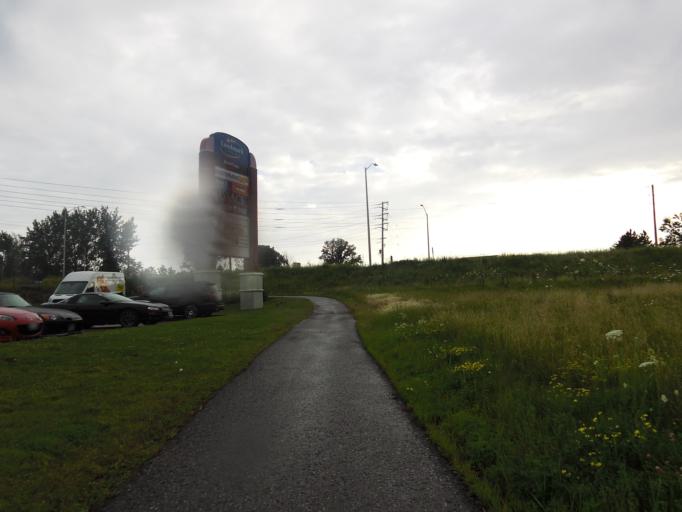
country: CA
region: Ontario
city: Bells Corners
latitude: 45.3083
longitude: -75.9140
